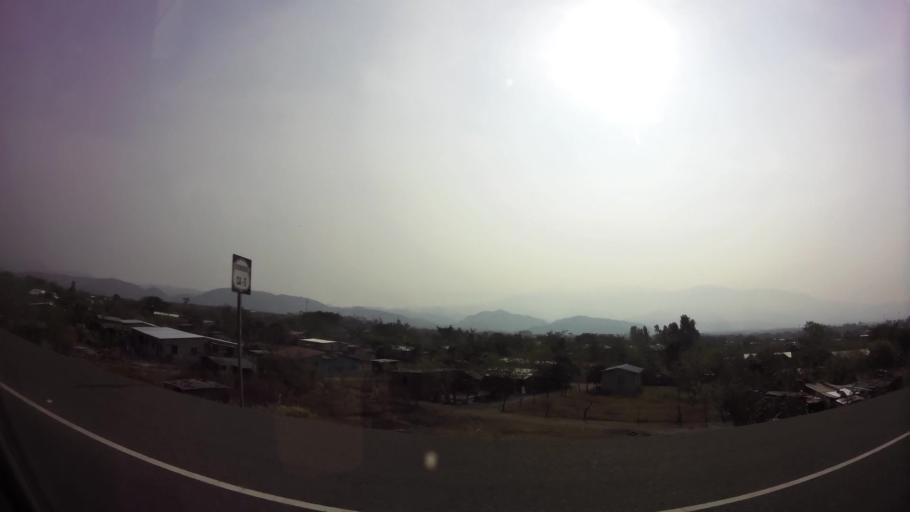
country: HN
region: Comayagua
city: Comayagua
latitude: 14.4596
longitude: -87.6674
